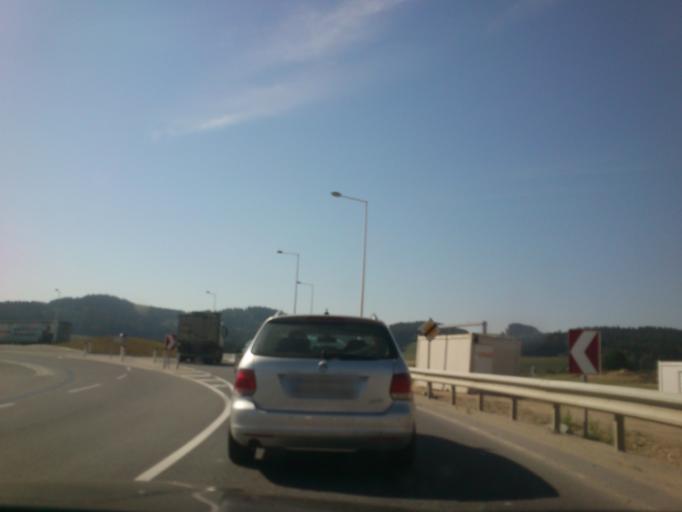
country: AT
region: Upper Austria
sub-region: Politischer Bezirk Freistadt
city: Freistadt
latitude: 48.4477
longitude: 14.4919
